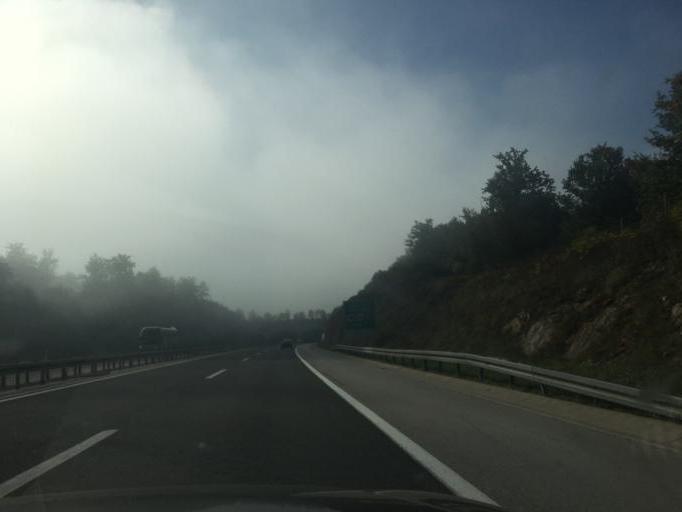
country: HR
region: Licko-Senjska
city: Gospic
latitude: 44.6351
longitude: 15.4393
